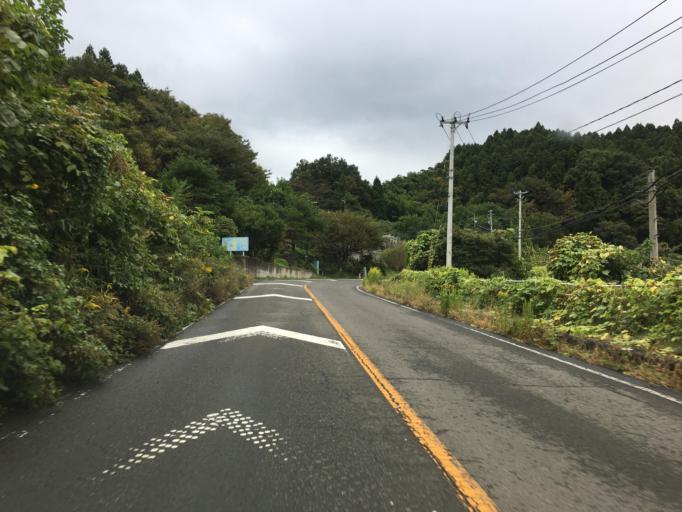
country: JP
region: Fukushima
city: Nihommatsu
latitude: 37.6131
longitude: 140.4418
